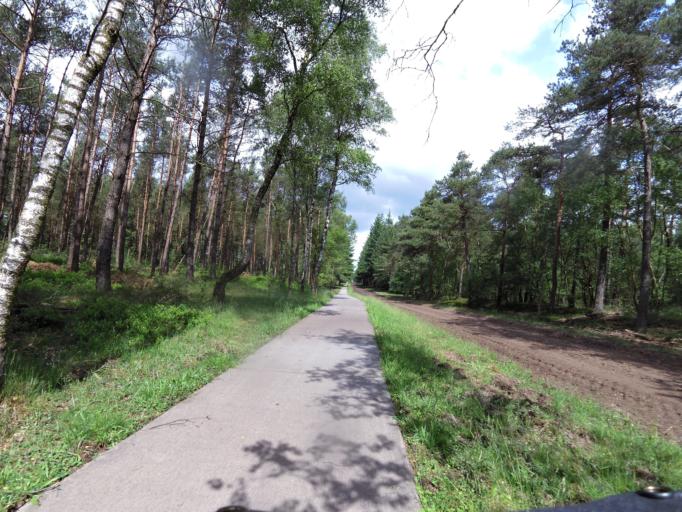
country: NL
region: Gelderland
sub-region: Gemeente Apeldoorn
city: Uddel
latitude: 52.3068
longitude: 5.7730
